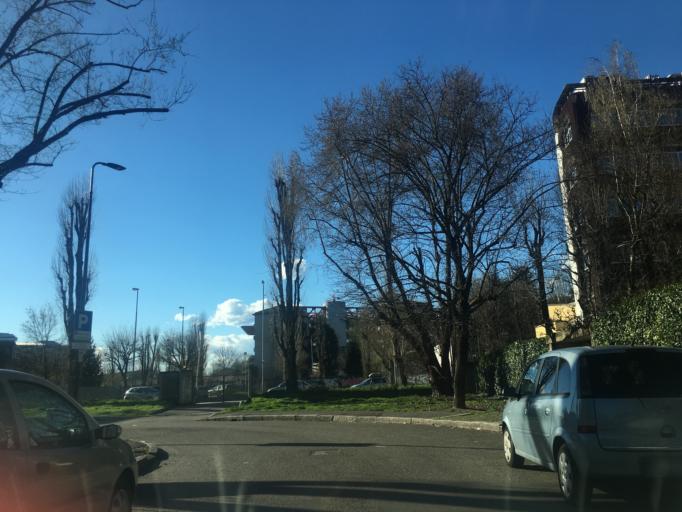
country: IT
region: Lombardy
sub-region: Citta metropolitana di Milano
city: Romano Banco
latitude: 45.4739
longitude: 9.1291
